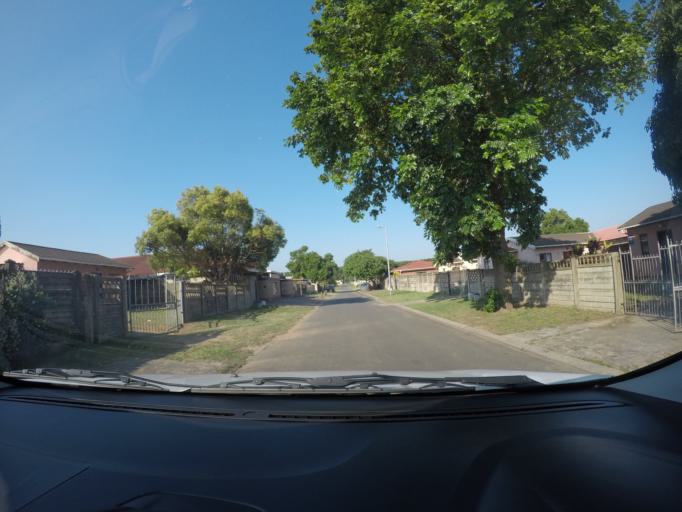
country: ZA
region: KwaZulu-Natal
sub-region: uThungulu District Municipality
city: Richards Bay
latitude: -28.7146
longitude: 32.0391
